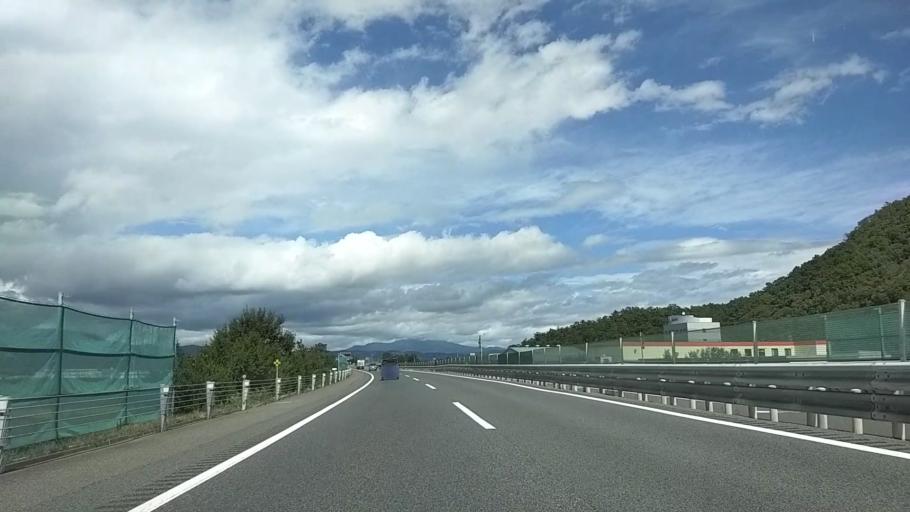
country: JP
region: Nagano
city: Suzaka
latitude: 36.6257
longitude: 138.2736
